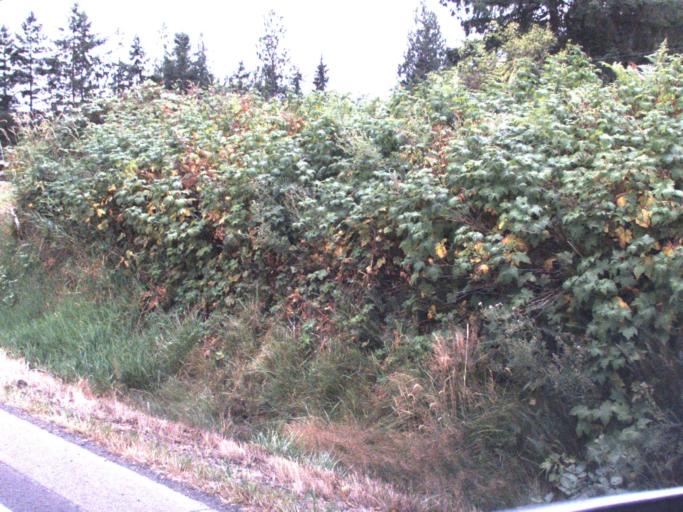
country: US
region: Washington
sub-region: King County
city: Carnation
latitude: 47.6225
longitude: -121.9098
